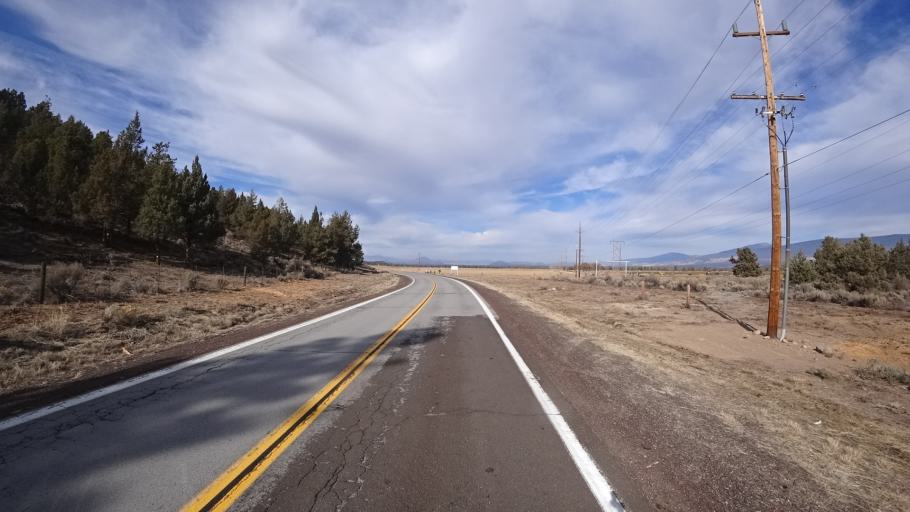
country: US
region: California
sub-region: Siskiyou County
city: Weed
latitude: 41.5395
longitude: -122.3653
